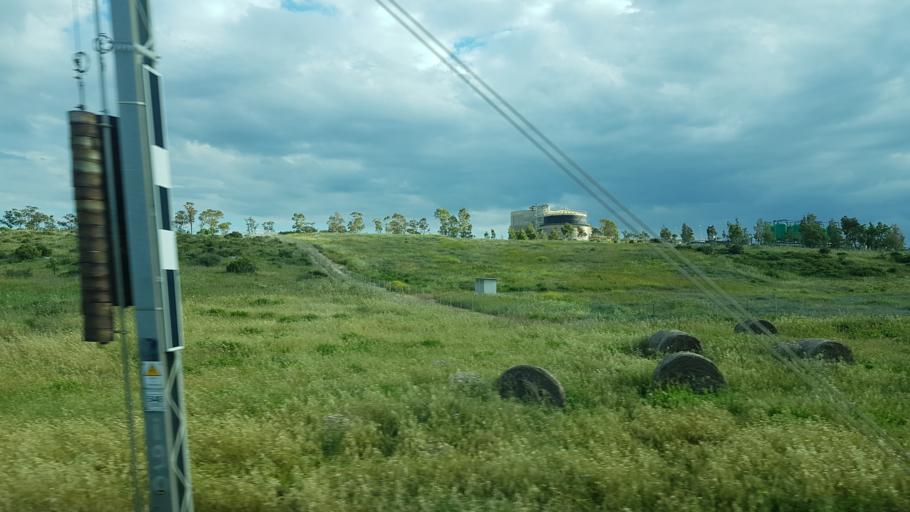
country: IT
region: Apulia
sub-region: Provincia di Brindisi
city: San Vito dei Normanni
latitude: 40.7190
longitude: 17.7481
